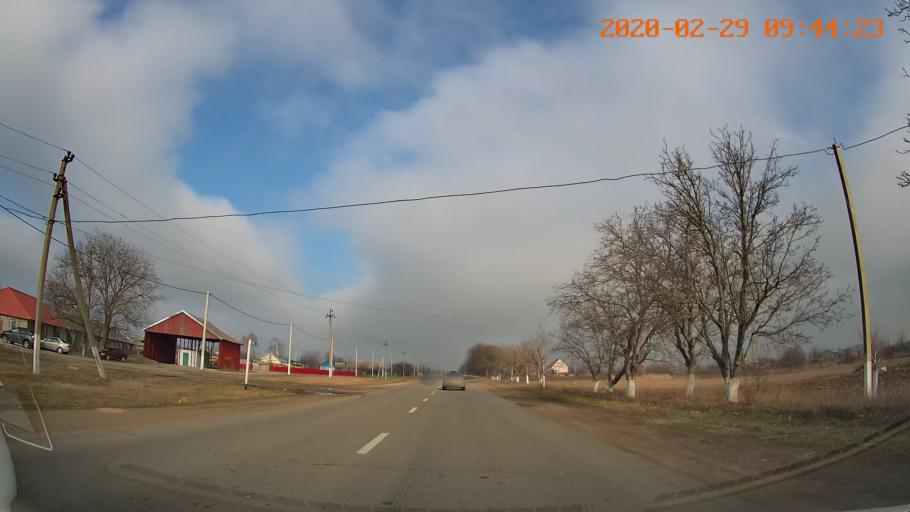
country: MD
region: Telenesti
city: Crasnoe
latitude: 46.6524
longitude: 29.8167
